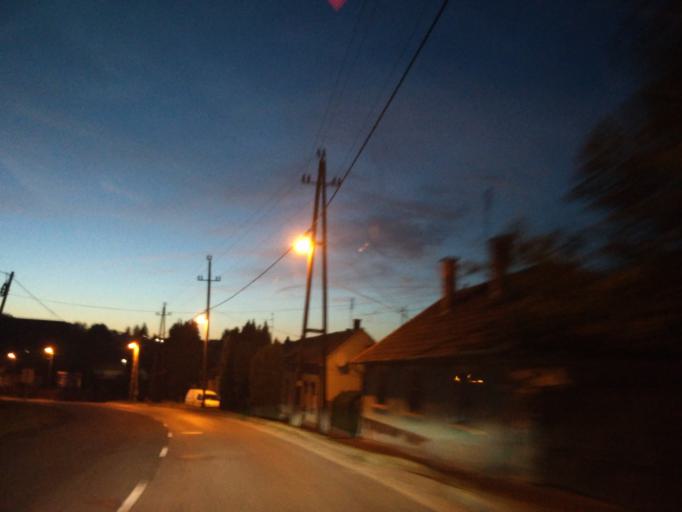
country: HU
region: Vas
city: Vasvar
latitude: 47.0459
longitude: 16.8076
